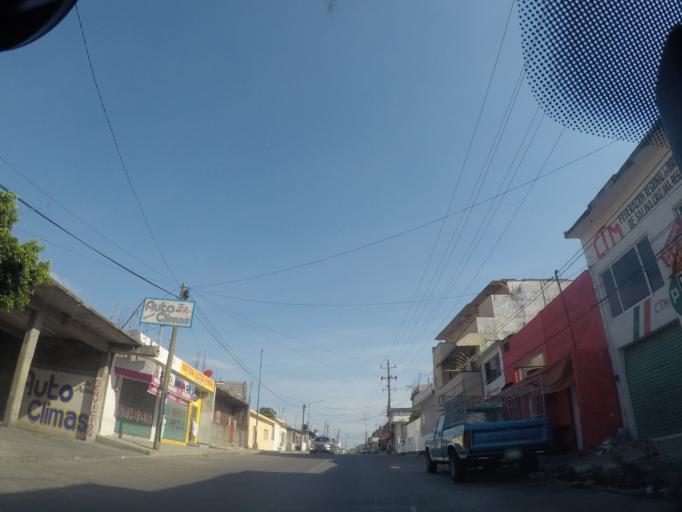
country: MX
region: Oaxaca
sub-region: Salina Cruz
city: Salina Cruz
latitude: 16.1960
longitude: -95.2027
